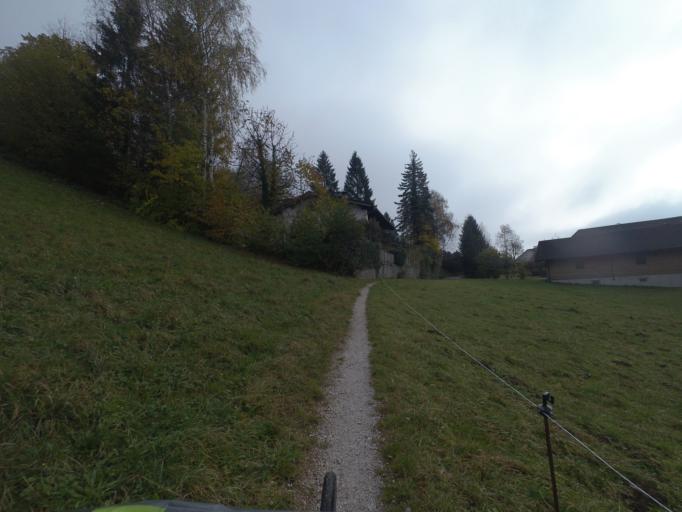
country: AT
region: Salzburg
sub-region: Politischer Bezirk Hallein
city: Adnet
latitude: 47.6693
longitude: 13.1375
